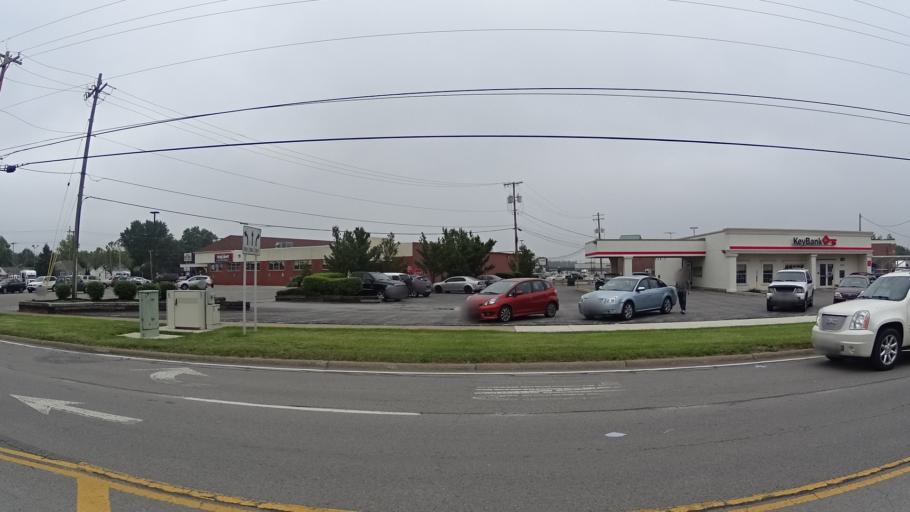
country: US
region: Ohio
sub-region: Erie County
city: Sandusky
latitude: 41.4314
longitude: -82.6972
